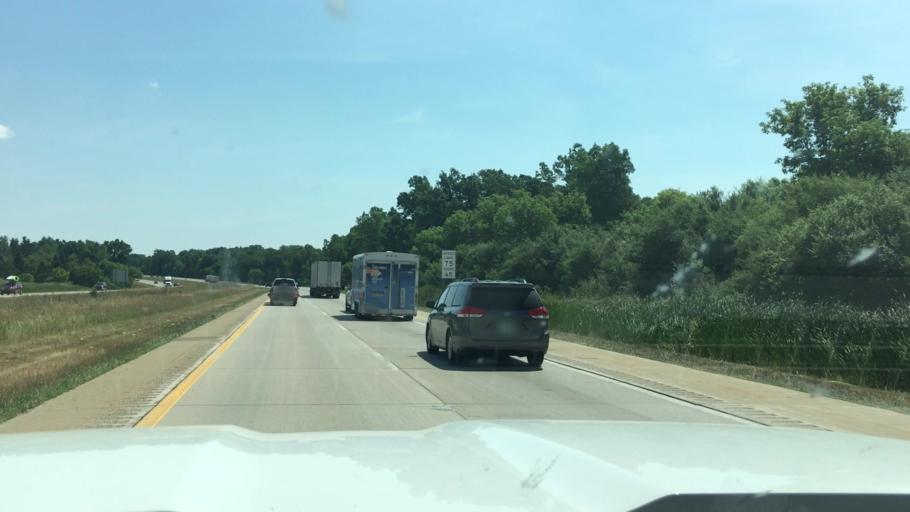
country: US
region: Michigan
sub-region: Ingham County
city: Haslett
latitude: 42.7811
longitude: -84.3958
